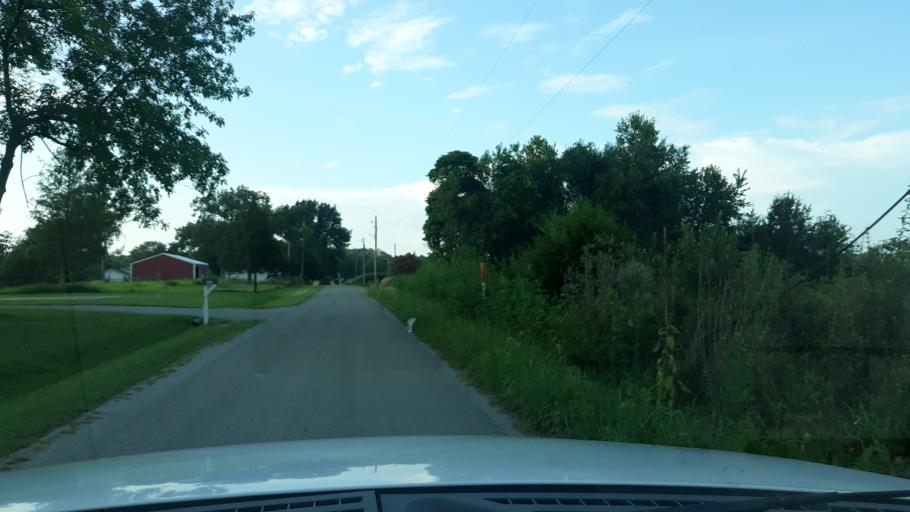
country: US
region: Illinois
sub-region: Saline County
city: Eldorado
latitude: 37.8300
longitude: -88.5166
